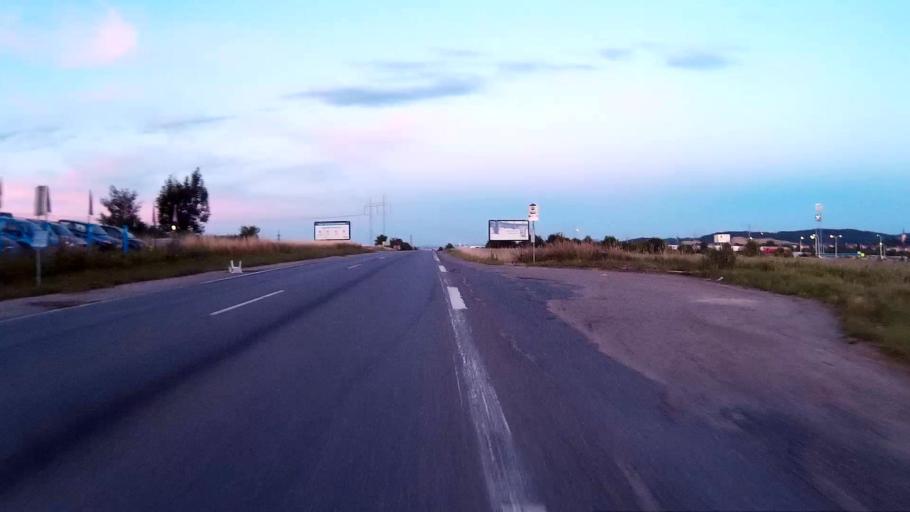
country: CZ
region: South Moravian
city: Troubsko
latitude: 49.1758
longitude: 16.5113
